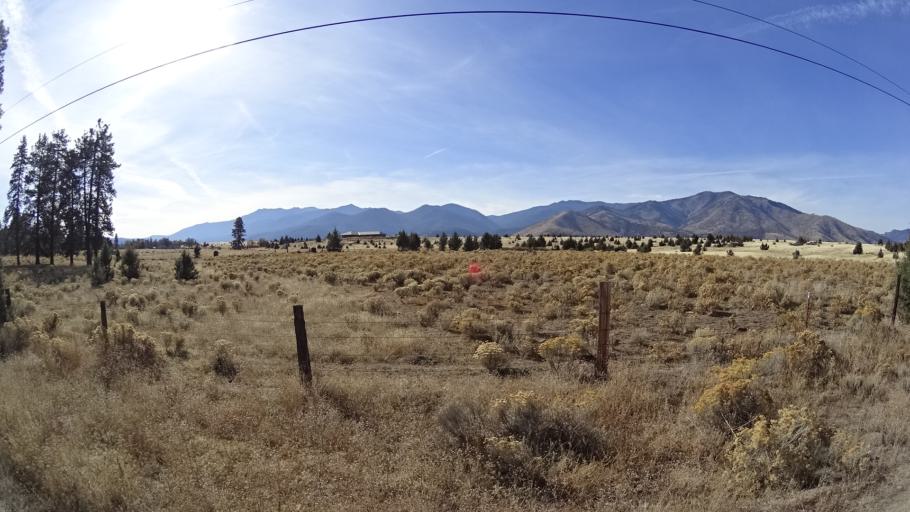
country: US
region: California
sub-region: Siskiyou County
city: Weed
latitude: 41.4879
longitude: -122.4454
